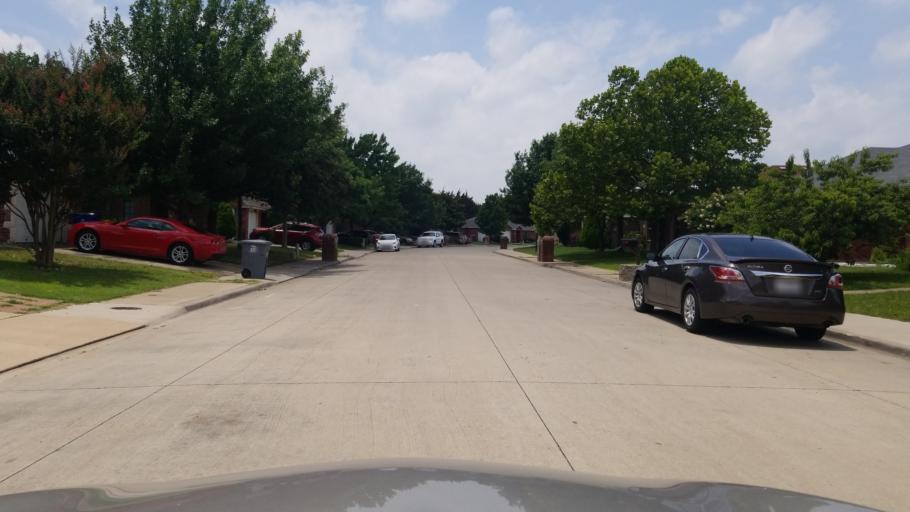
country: US
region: Texas
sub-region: Dallas County
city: Duncanville
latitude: 32.6856
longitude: -96.9169
